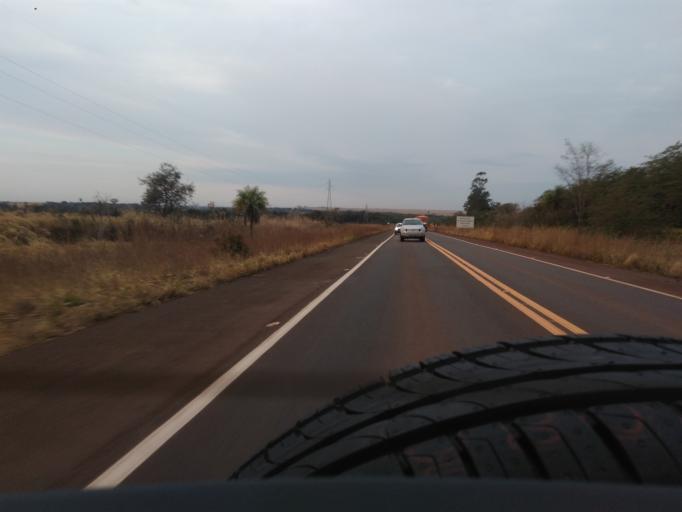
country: BR
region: Mato Grosso do Sul
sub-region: Dourados
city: Dourados
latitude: -22.2956
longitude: -55.0698
